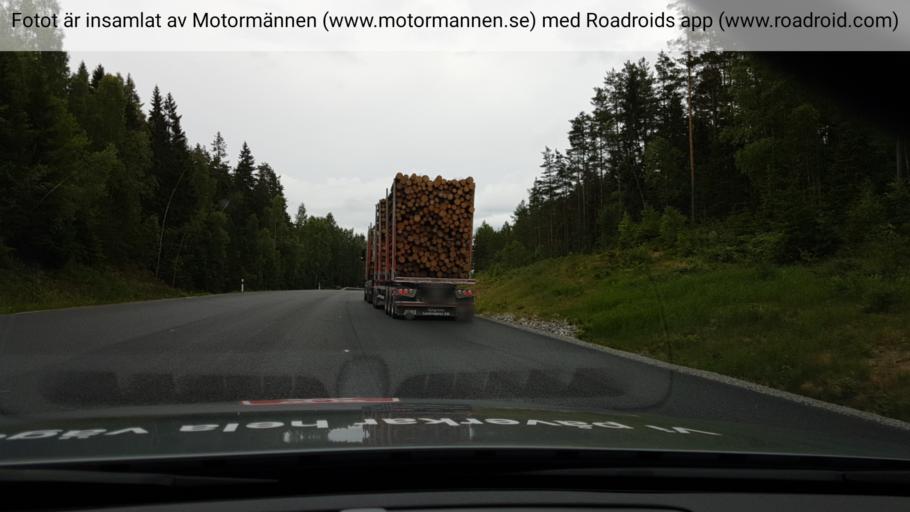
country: SE
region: Vaestmanland
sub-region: Skinnskattebergs Kommun
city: Skinnskatteberg
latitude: 59.8285
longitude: 15.5362
